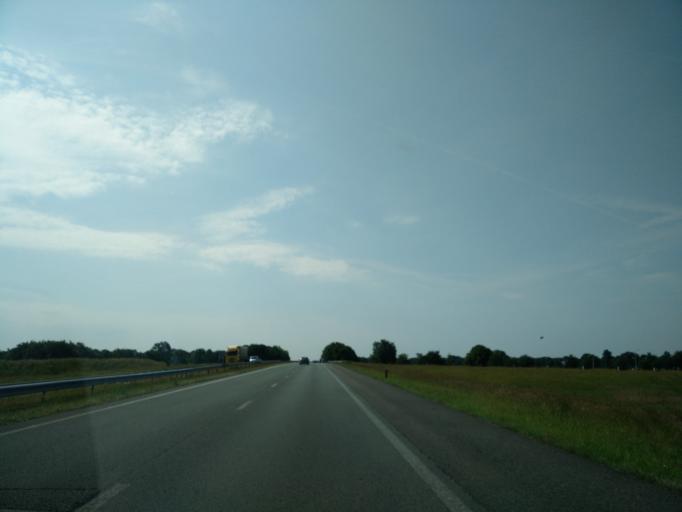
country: NL
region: Drenthe
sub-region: Gemeente Tynaarlo
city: Tynaarlo
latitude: 53.0826
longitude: 6.6037
